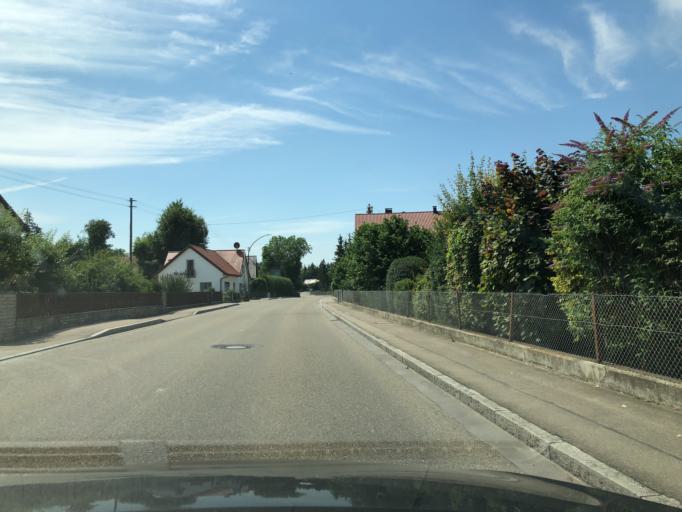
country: DE
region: Bavaria
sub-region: Swabia
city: Oberndorf
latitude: 48.6695
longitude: 10.8724
